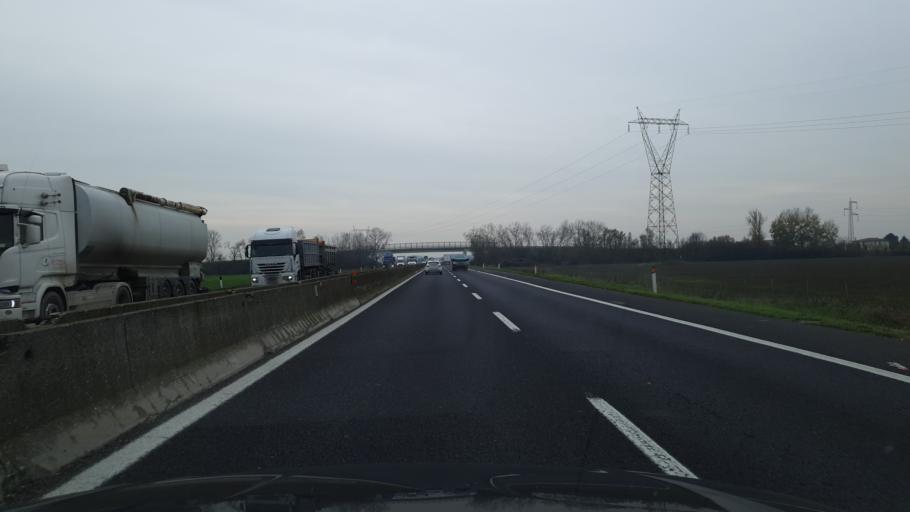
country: IT
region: Emilia-Romagna
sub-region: Provincia di Ferrara
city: San Martino
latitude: 44.7756
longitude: 11.5458
